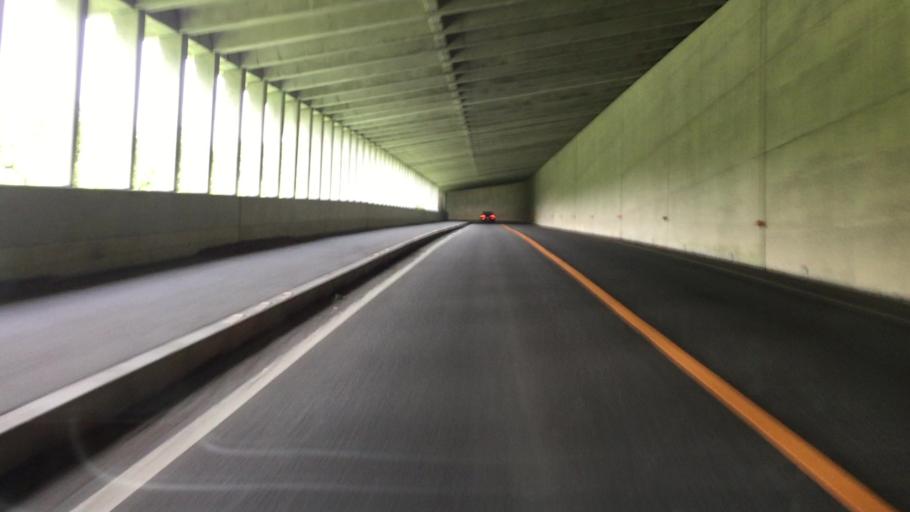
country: JP
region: Tochigi
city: Kuroiso
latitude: 37.0487
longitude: 139.9316
